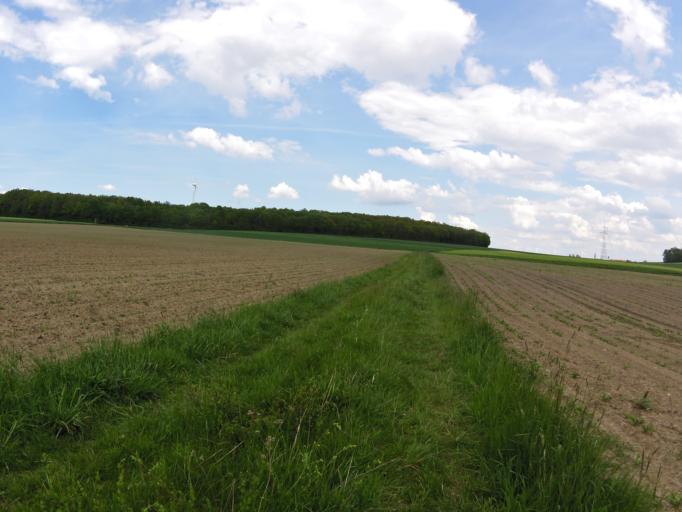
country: DE
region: Bavaria
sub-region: Regierungsbezirk Unterfranken
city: Theilheim
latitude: 49.7401
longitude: 10.0391
